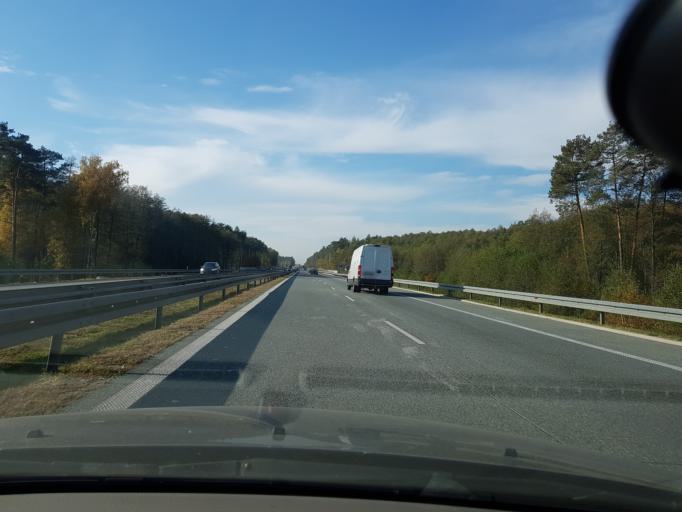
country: PL
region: Lodz Voivodeship
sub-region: Powiat tomaszowski
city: Czerniewice
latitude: 51.6339
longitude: 20.1118
